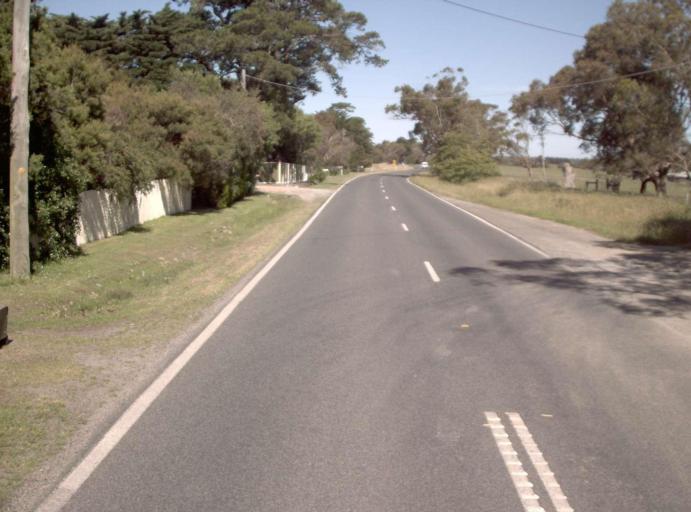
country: AU
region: Victoria
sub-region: Latrobe
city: Morwell
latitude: -38.6690
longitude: 146.3794
